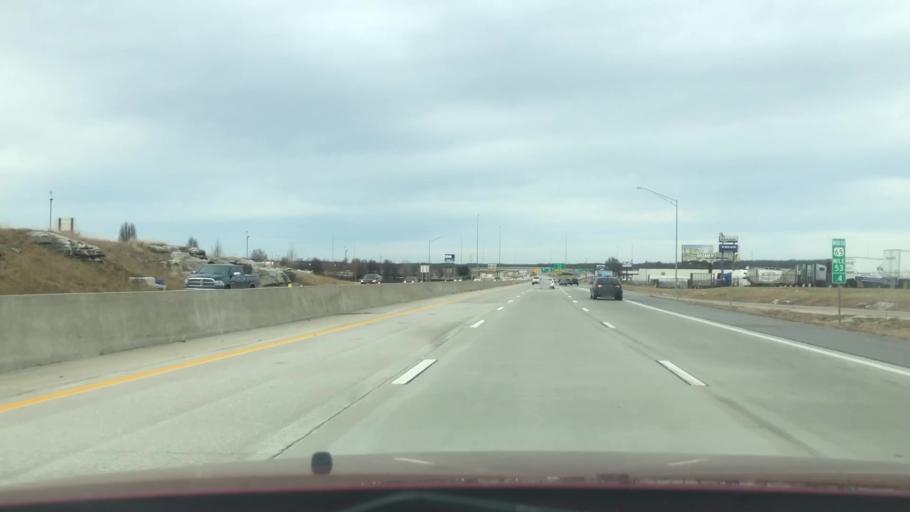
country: US
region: Missouri
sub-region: Greene County
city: Springfield
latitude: 37.2402
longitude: -93.2246
